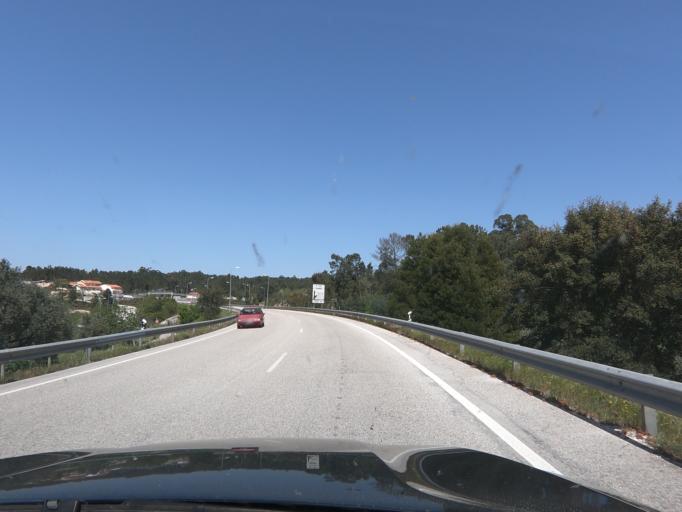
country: PT
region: Coimbra
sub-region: Miranda do Corvo
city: Miranda do Corvo
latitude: 40.0887
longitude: -8.3182
